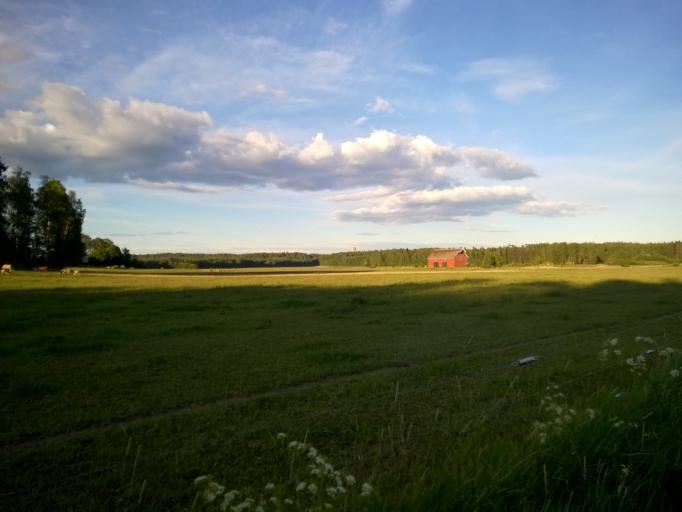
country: FI
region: Uusimaa
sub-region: Helsinki
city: Vantaa
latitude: 60.2195
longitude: 25.0107
